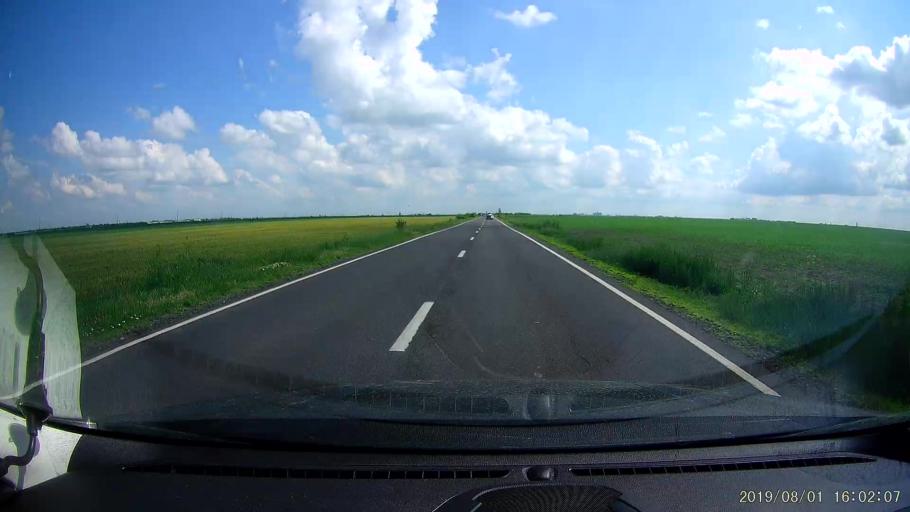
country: RO
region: Ialomita
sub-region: Comuna Ciulnita
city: Ciulnita
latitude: 44.4958
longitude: 27.3883
